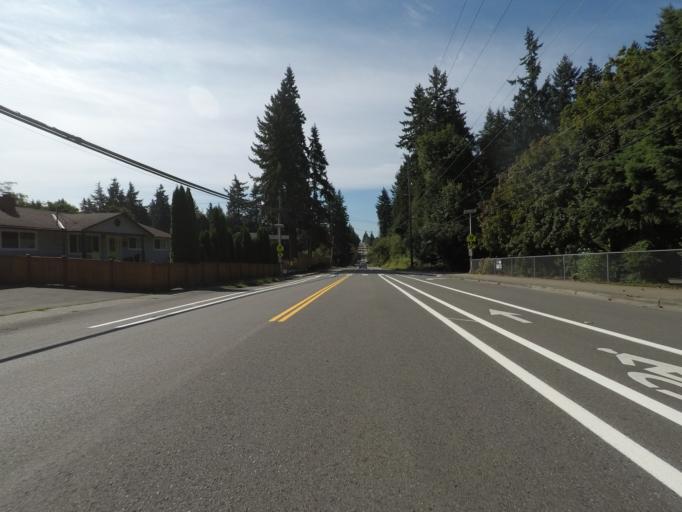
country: US
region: Washington
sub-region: King County
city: Inglewood-Finn Hill
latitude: 47.7247
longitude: -122.2293
